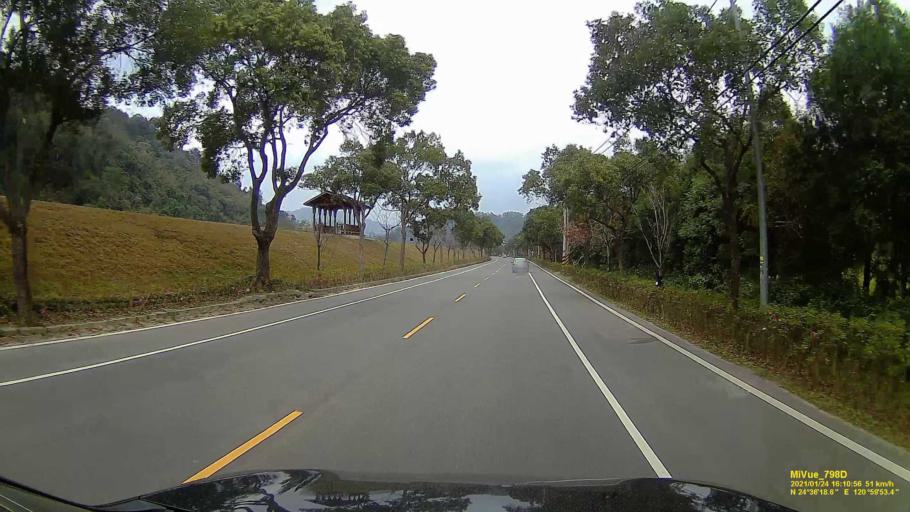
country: TW
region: Taiwan
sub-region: Miaoli
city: Miaoli
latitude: 24.6053
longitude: 120.9983
